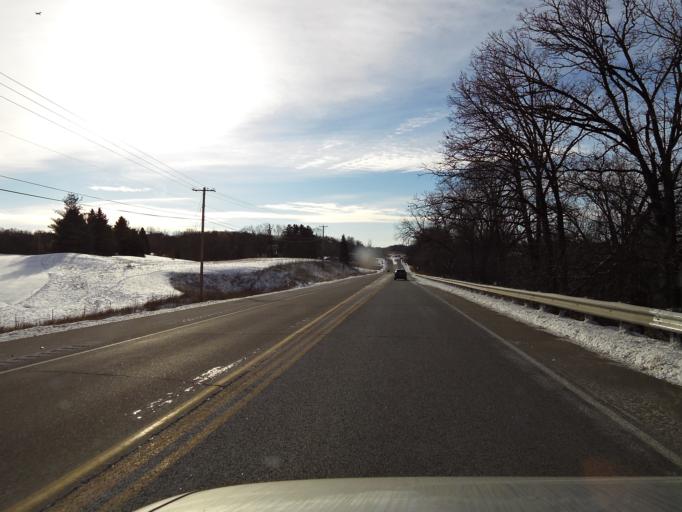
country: US
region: Minnesota
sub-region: Dakota County
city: Inver Grove Heights
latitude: 44.8433
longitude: -93.0854
